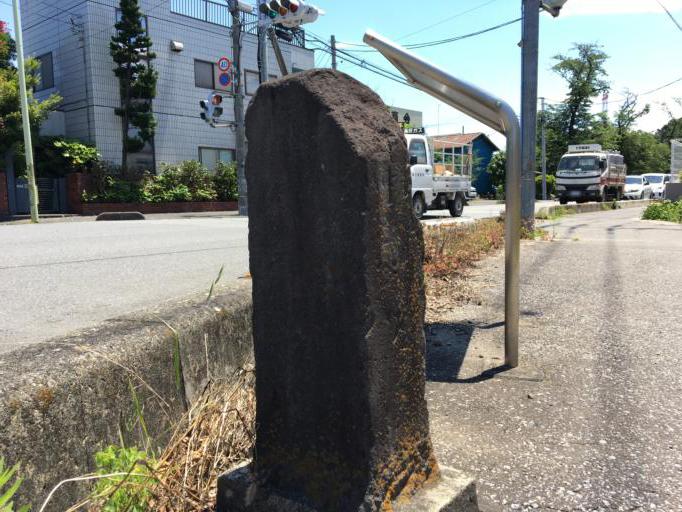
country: JP
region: Saitama
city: Sakado
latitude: 35.9374
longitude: 139.3882
